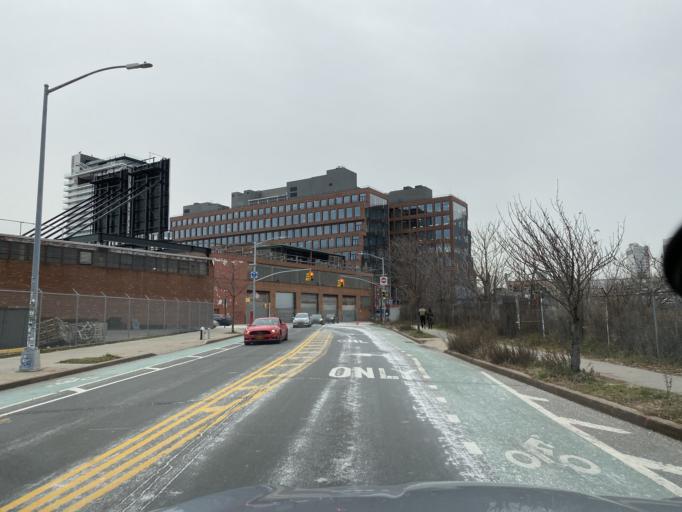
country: US
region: New York
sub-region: Queens County
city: Long Island City
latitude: 40.7248
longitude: -73.9577
